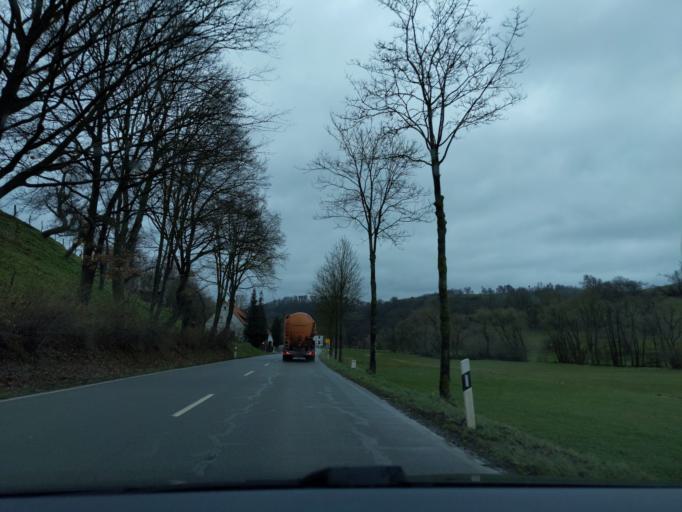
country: DE
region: Hesse
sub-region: Regierungsbezirk Kassel
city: Bad Arolsen
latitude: 51.3170
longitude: 9.0083
